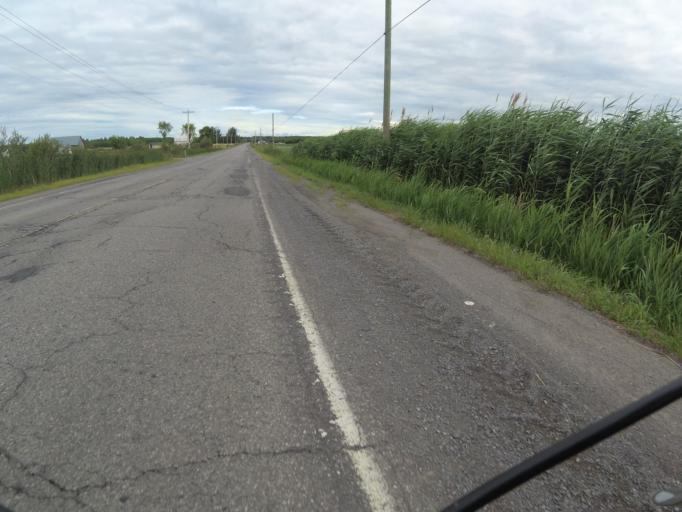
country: CA
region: Ontario
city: Bourget
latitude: 45.3783
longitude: -75.2718
